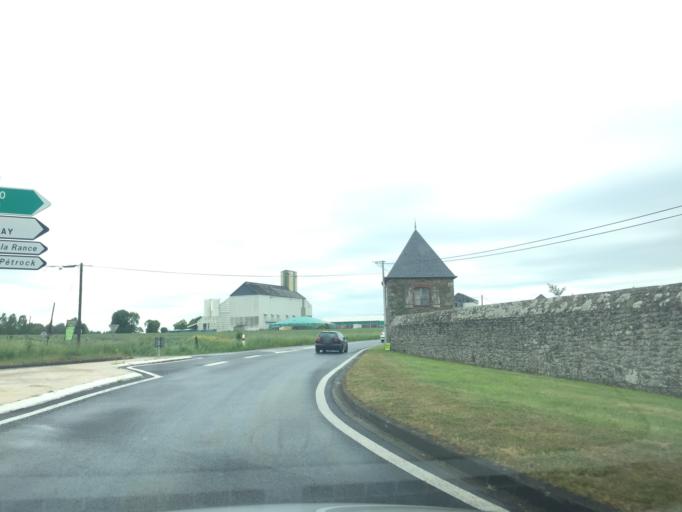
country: FR
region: Brittany
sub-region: Departement des Cotes-d'Armor
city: Crehen
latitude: 48.5653
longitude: -2.1893
